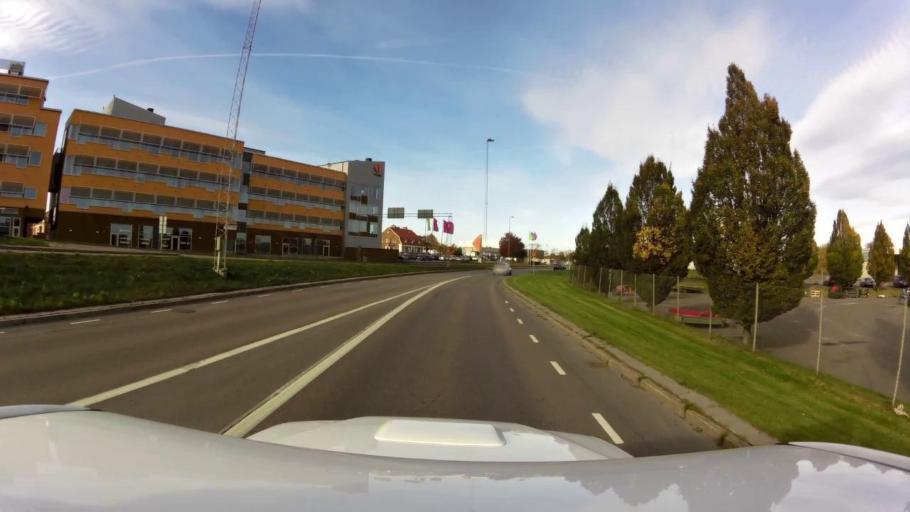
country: SE
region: OEstergoetland
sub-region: Linkopings Kommun
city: Linkoping
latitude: 58.4225
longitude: 15.6170
